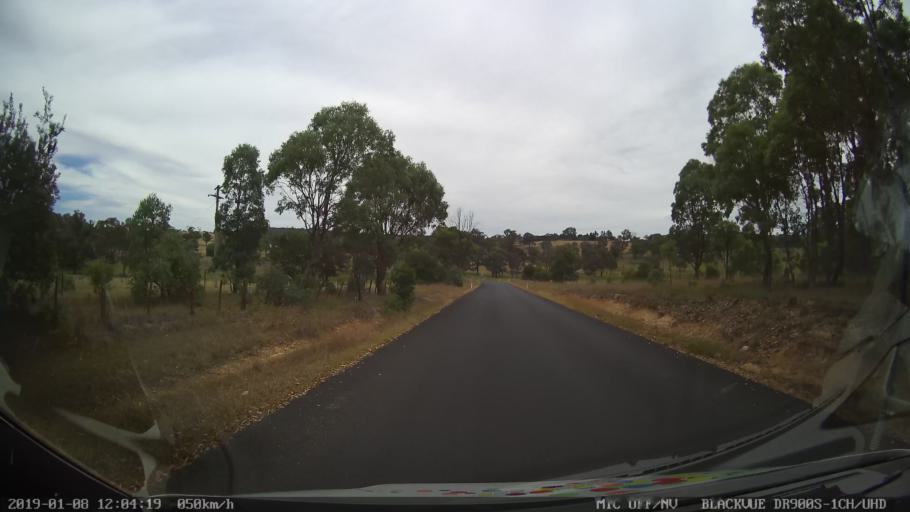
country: AU
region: New South Wales
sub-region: Armidale Dumaresq
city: Armidale
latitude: -30.4442
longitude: 151.5898
